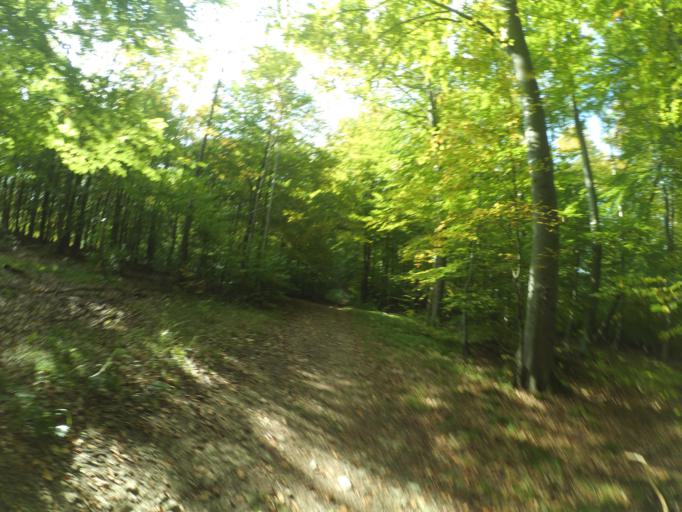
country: DE
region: Baden-Wuerttemberg
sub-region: Regierungsbezirk Stuttgart
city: Heubach
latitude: 48.7793
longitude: 9.9077
